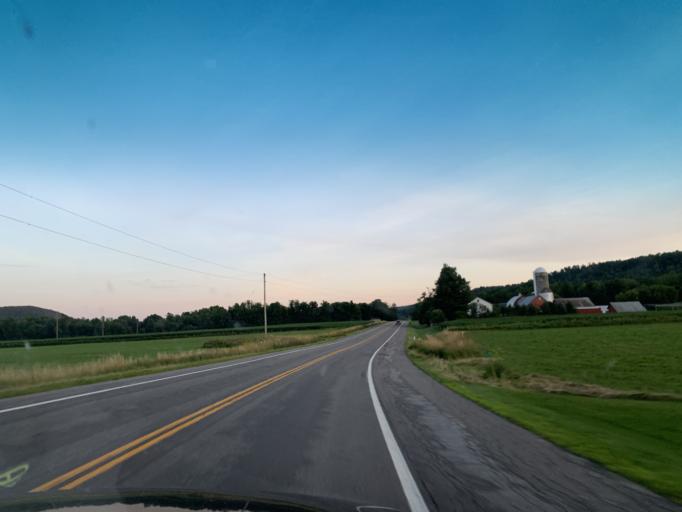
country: US
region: New York
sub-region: Oneida County
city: Waterville
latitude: 42.8656
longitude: -75.2496
